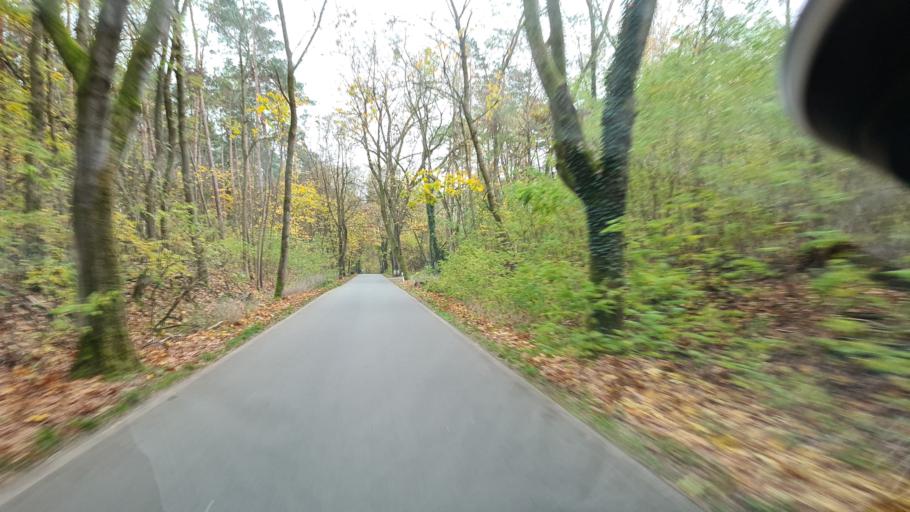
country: DE
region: Brandenburg
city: Lindow
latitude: 52.9575
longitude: 12.9853
